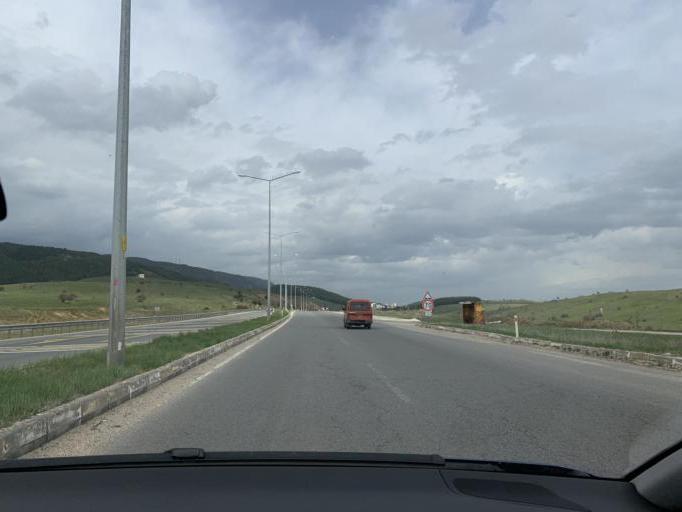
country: TR
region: Bolu
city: Gerede
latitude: 40.7962
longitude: 32.1558
